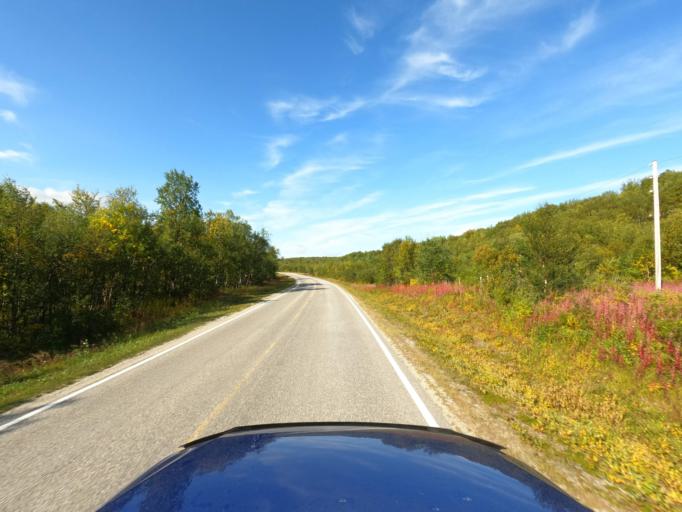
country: NO
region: Finnmark Fylke
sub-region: Porsanger
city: Lakselv
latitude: 69.7618
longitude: 25.2020
